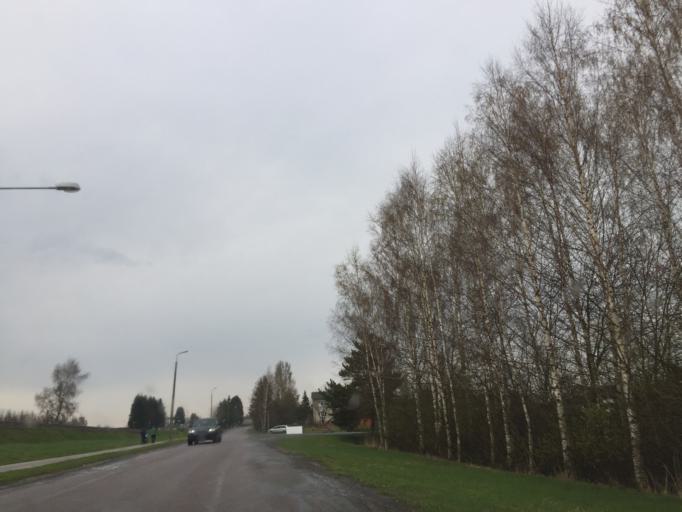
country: EE
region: Tartu
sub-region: UElenurme vald
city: Ulenurme
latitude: 58.3079
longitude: 26.7225
